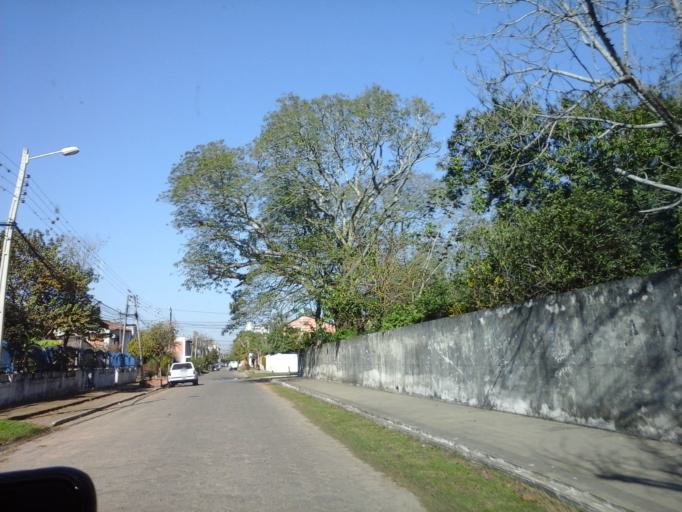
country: PY
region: Neembucu
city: Pilar
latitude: -26.8532
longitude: -58.3070
